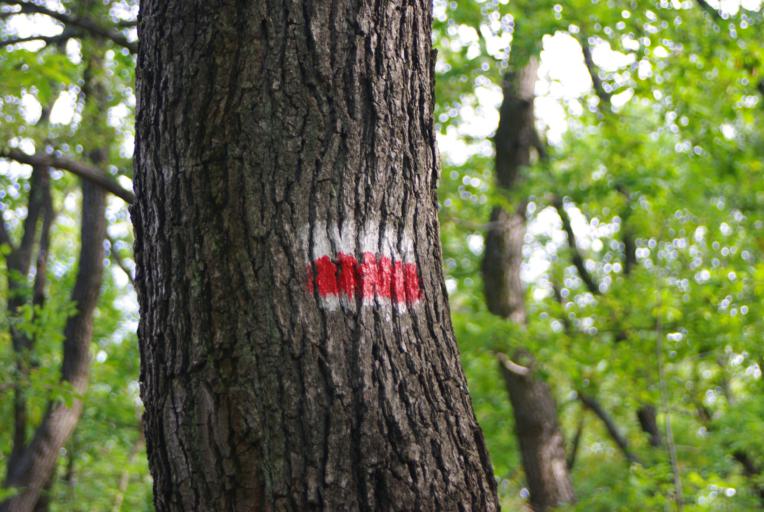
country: HU
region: Pest
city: Csobanka
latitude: 47.6721
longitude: 18.9641
